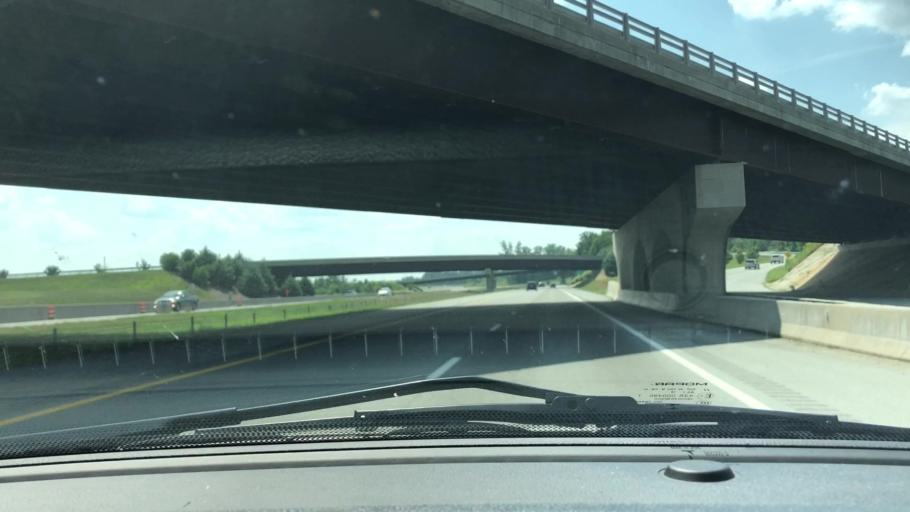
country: US
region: North Carolina
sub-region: Guilford County
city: Oak Ridge
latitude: 36.1224
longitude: -79.9288
